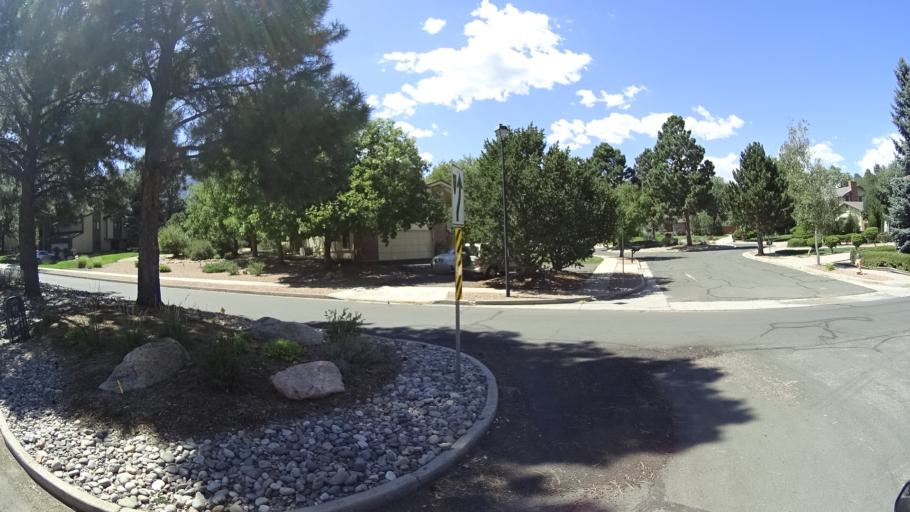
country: US
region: Colorado
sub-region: El Paso County
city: Colorado Springs
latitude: 38.7880
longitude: -104.8276
